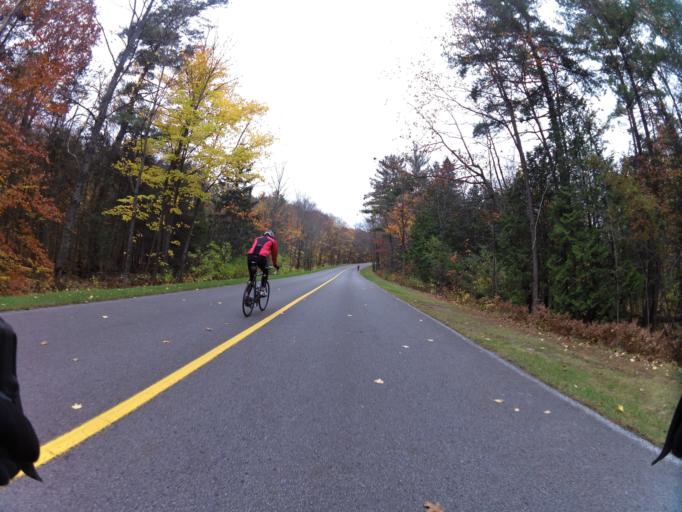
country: CA
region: Quebec
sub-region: Outaouais
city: Gatineau
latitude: 45.4504
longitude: -75.7692
